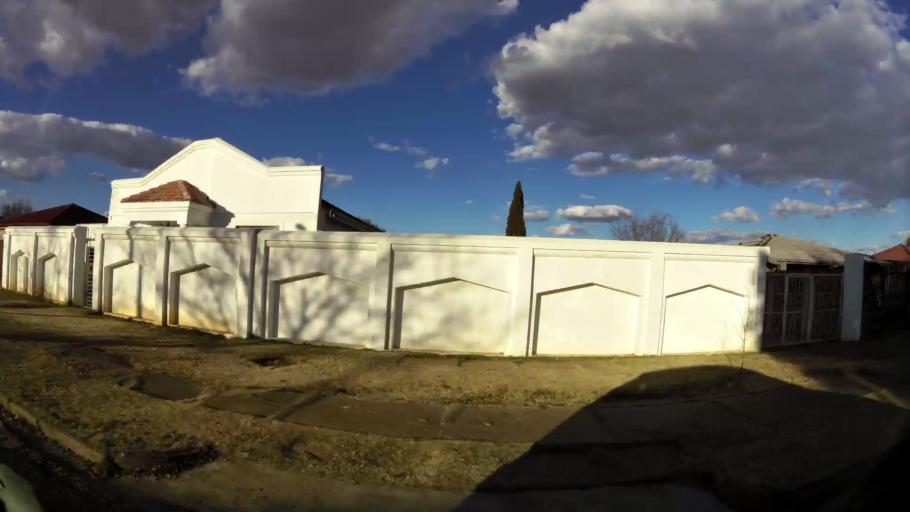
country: ZA
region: North-West
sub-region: Dr Kenneth Kaunda District Municipality
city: Potchefstroom
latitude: -26.7183
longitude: 27.1008
